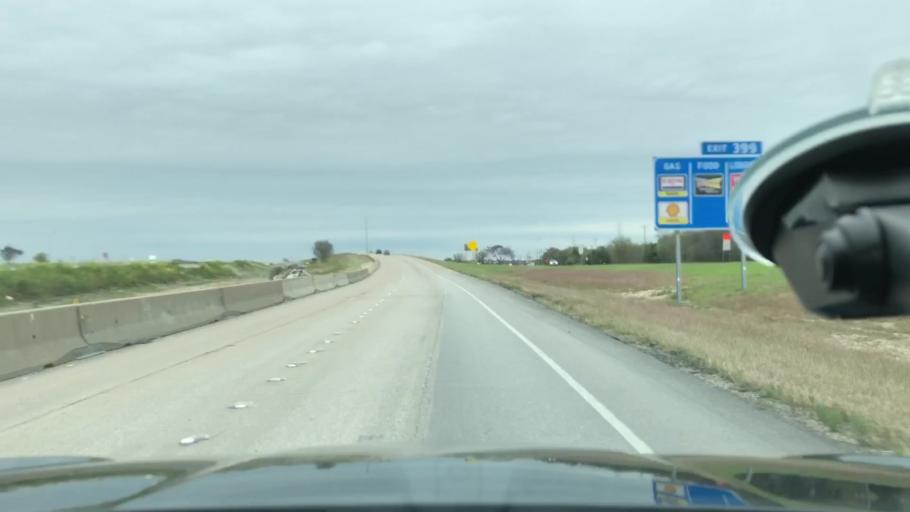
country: US
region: Texas
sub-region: Ellis County
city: Waxahachie
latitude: 32.3594
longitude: -96.8548
